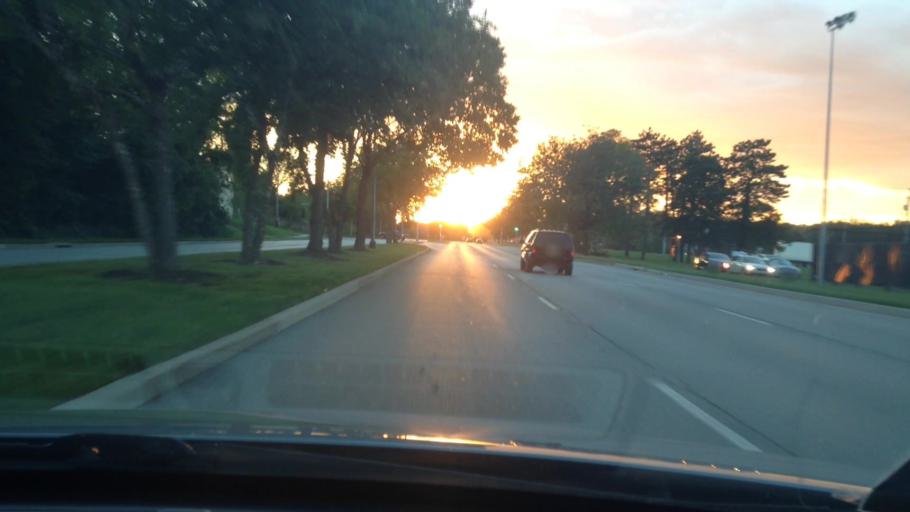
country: US
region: Kansas
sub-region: Johnson County
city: Westwood
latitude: 39.0411
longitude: -94.5619
